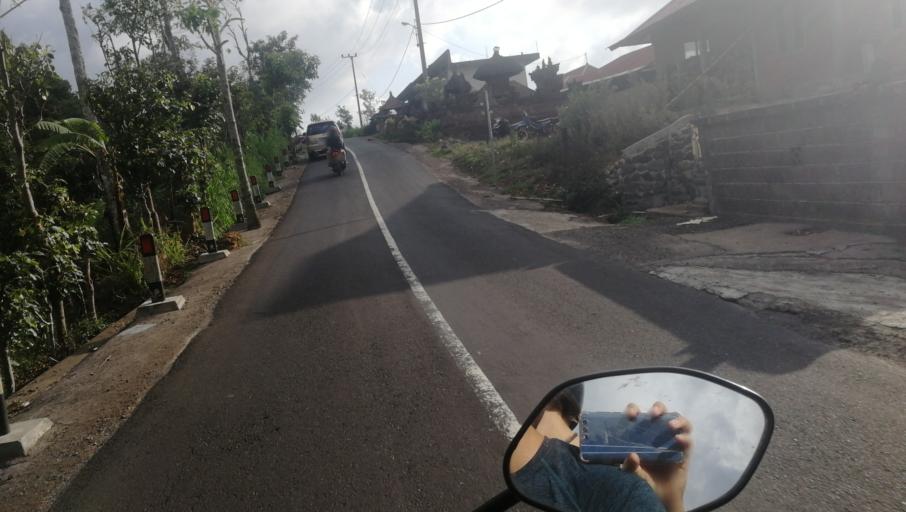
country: ID
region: Bali
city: Munduk
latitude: -8.2589
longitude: 115.0896
